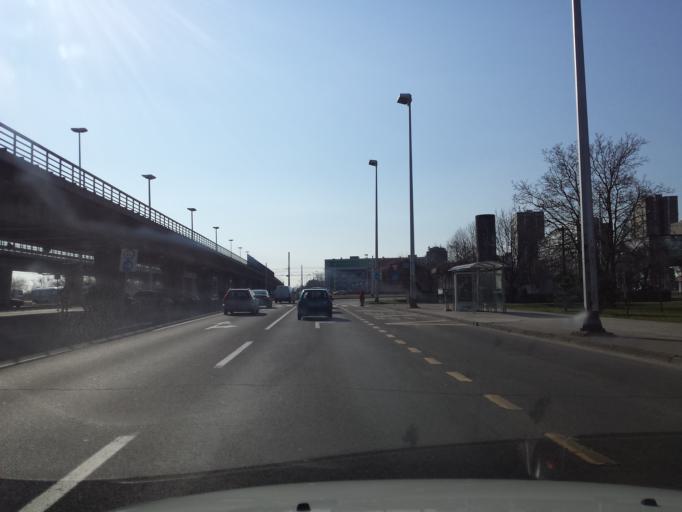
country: HR
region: Grad Zagreb
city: Novi Zagreb
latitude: 45.7792
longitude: 16.0014
